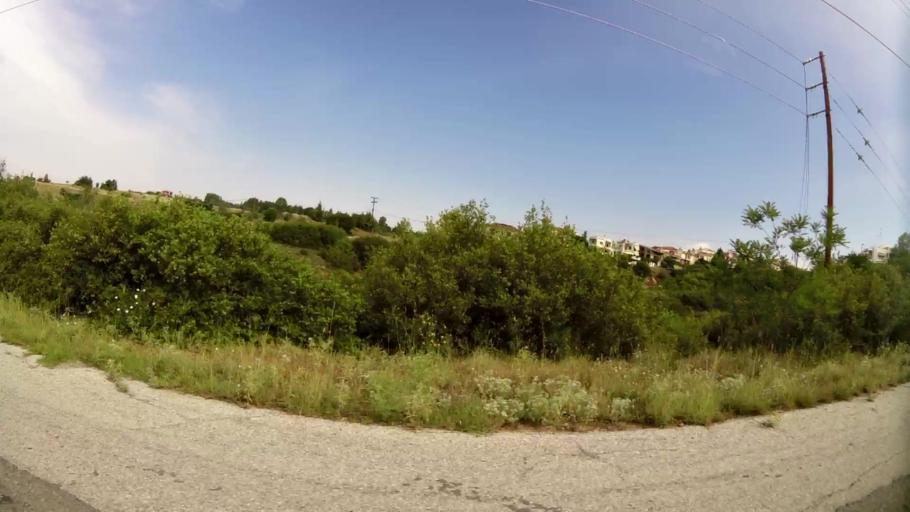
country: GR
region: Central Macedonia
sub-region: Nomos Thessalonikis
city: Panorama
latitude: 40.5768
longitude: 23.0074
